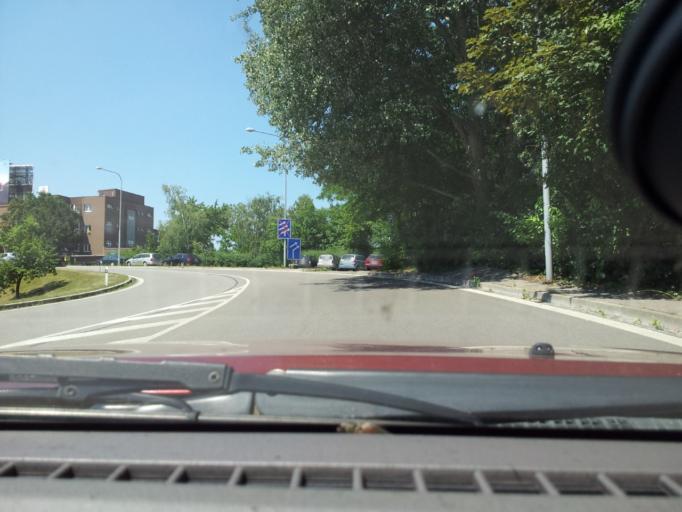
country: CZ
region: South Moravian
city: Moravany
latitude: 49.1637
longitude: 16.6006
